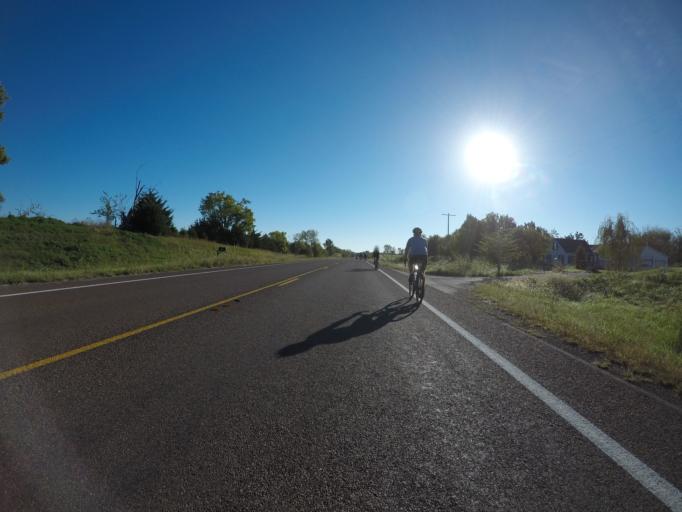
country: US
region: Kansas
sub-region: Douglas County
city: Eudora
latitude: 39.0005
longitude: -95.1558
